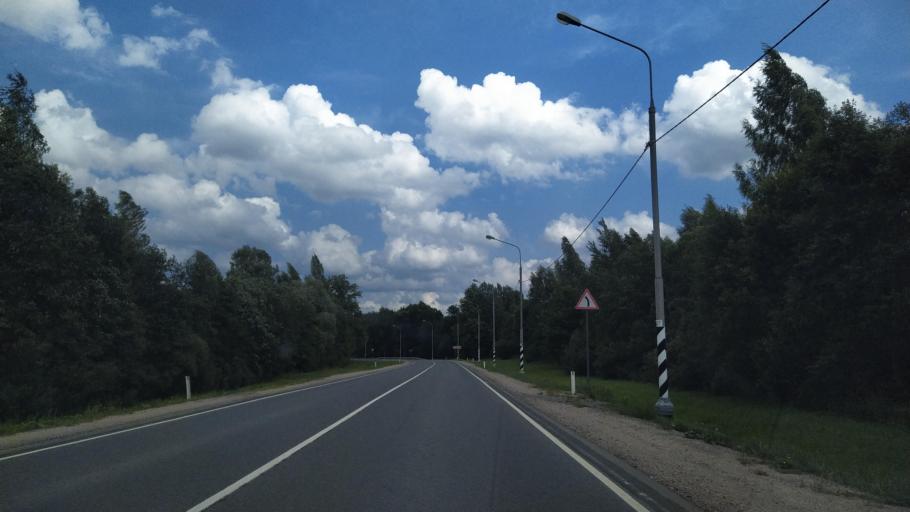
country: RU
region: Pskov
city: Dno
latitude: 58.0515
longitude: 29.9483
